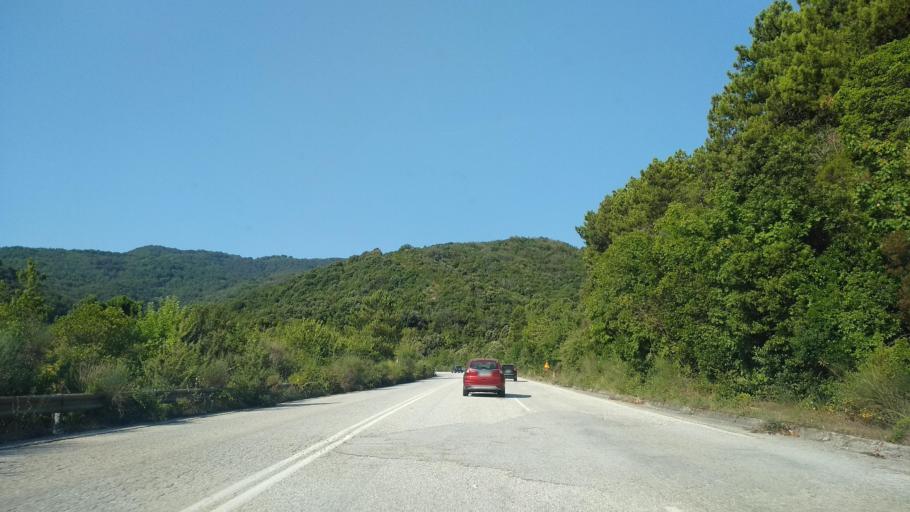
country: GR
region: Central Macedonia
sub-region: Nomos Chalkidikis
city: Stratonion
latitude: 40.5527
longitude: 23.8250
